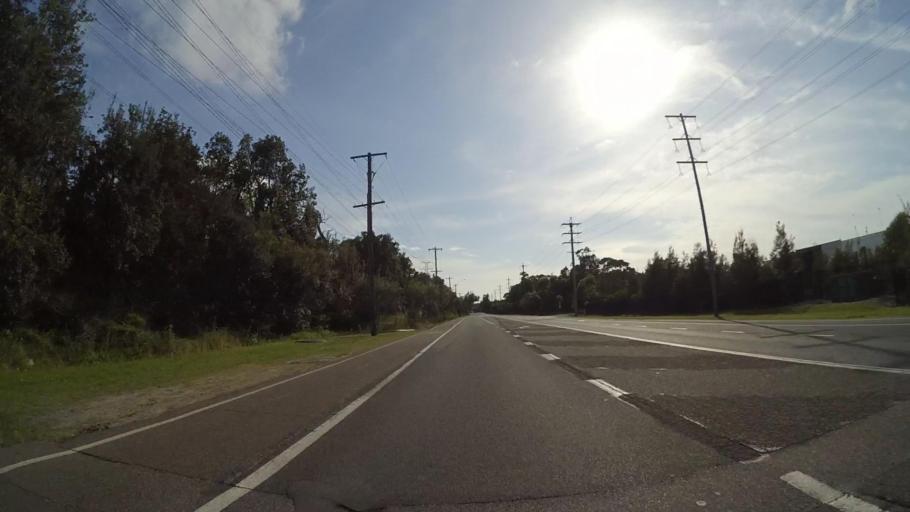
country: AU
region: New South Wales
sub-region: Sutherland Shire
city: Kurnell
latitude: -34.0209
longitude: 151.1995
